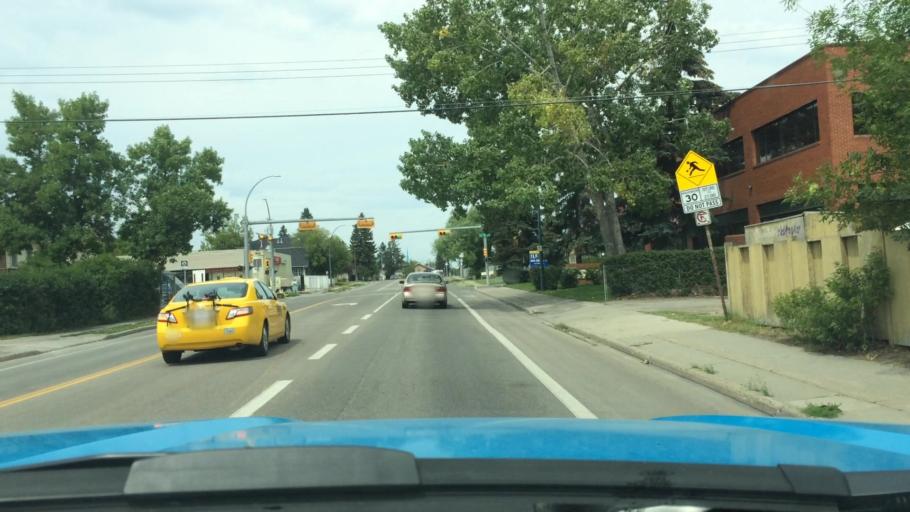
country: CA
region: Alberta
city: Calgary
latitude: 51.0699
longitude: -114.0848
